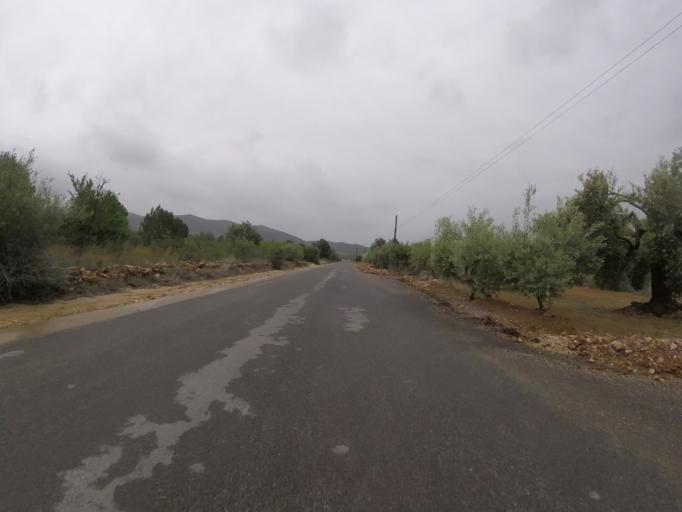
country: ES
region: Valencia
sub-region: Provincia de Castello
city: Alcala de Xivert
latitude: 40.2714
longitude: 0.2381
